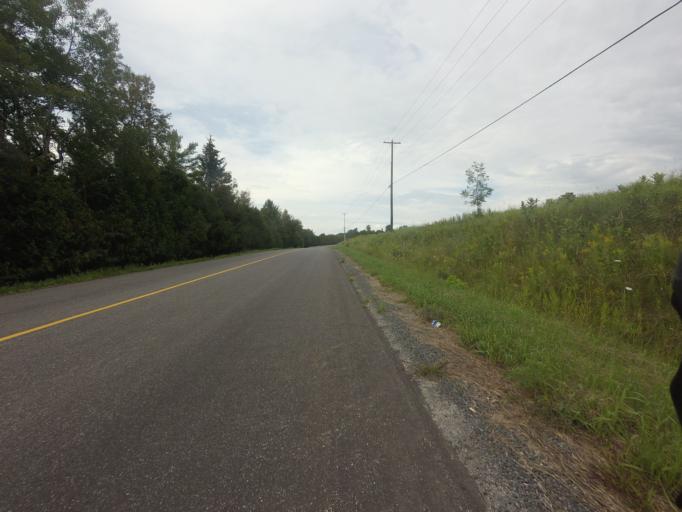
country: CA
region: Ontario
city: Perth
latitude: 45.0893
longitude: -76.3998
